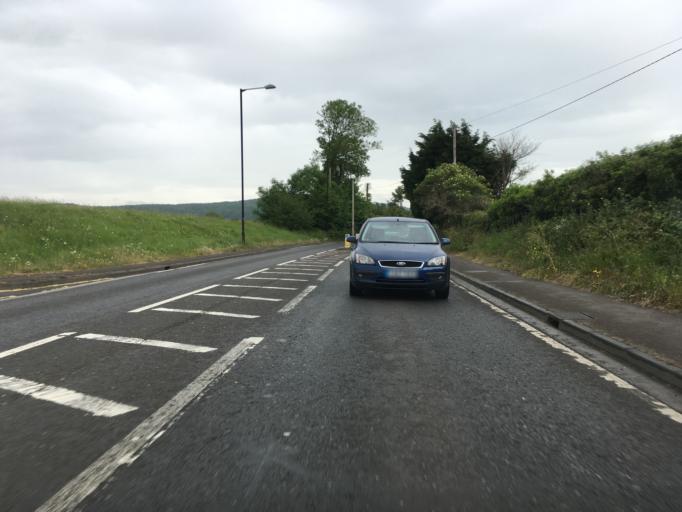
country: GB
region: England
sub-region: North Somerset
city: Congresbury
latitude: 51.3718
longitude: -2.8173
